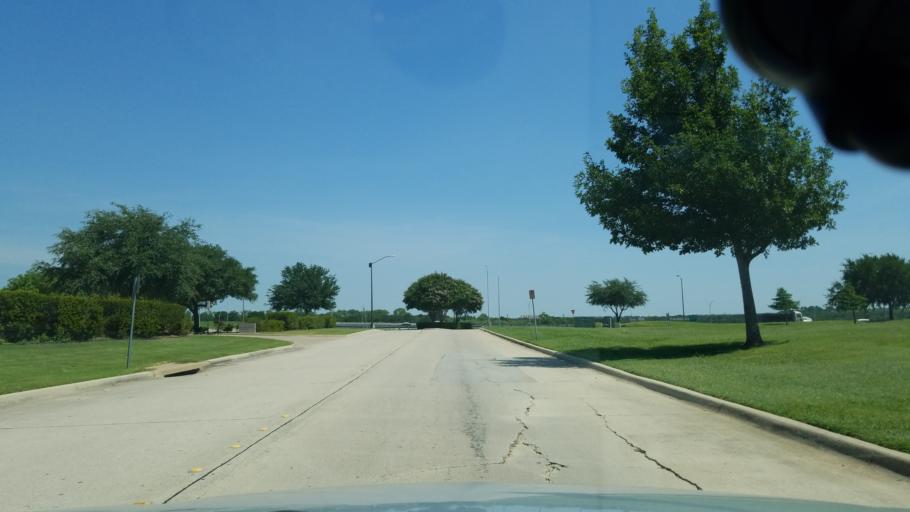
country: US
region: Texas
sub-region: Tarrant County
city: Euless
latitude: 32.8345
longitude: -97.0462
